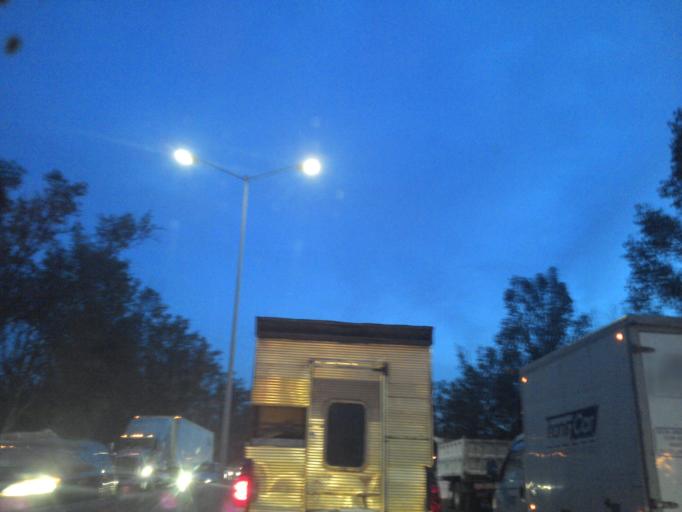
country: MX
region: Jalisco
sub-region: Tlajomulco de Zuniga
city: Palomar
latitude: 20.6230
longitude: -103.4324
